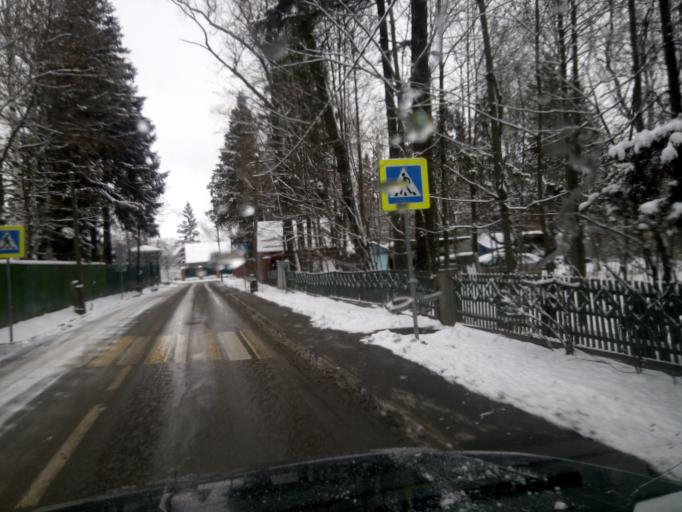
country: RU
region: Moskovskaya
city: Skhodnya
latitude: 55.9494
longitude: 37.3104
